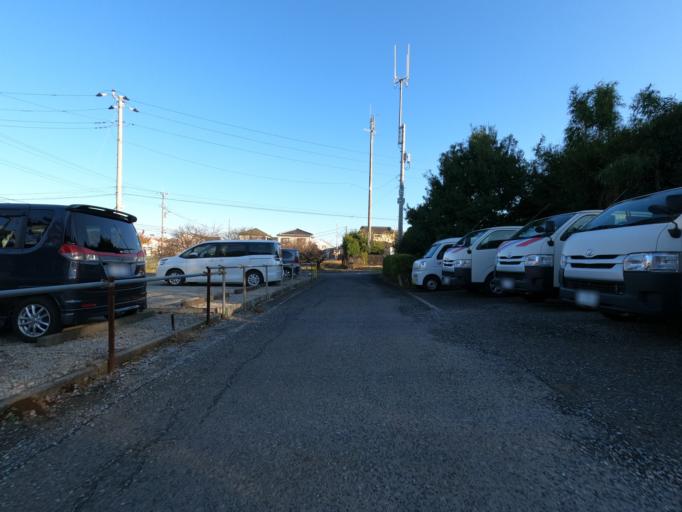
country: JP
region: Ibaraki
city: Moriya
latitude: 35.9326
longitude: 140.0002
